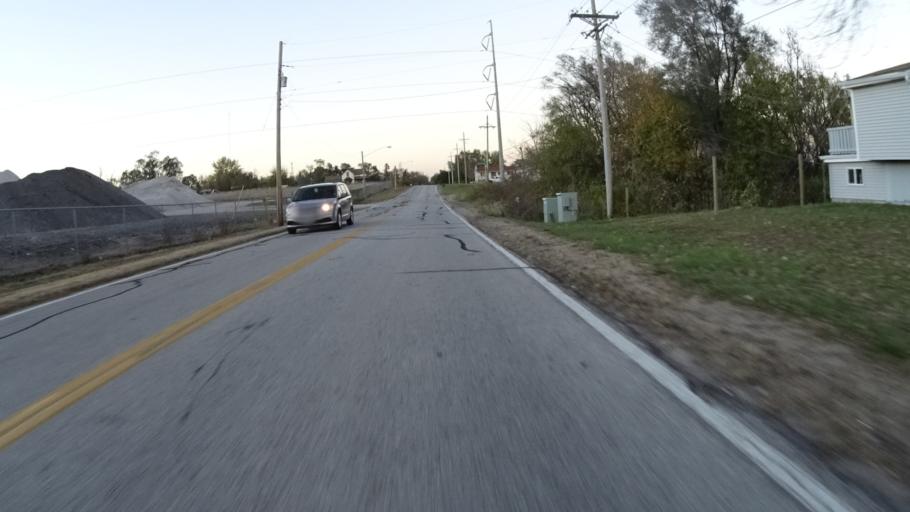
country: US
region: Nebraska
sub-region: Sarpy County
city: Offutt Air Force Base
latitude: 41.1711
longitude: -95.9527
